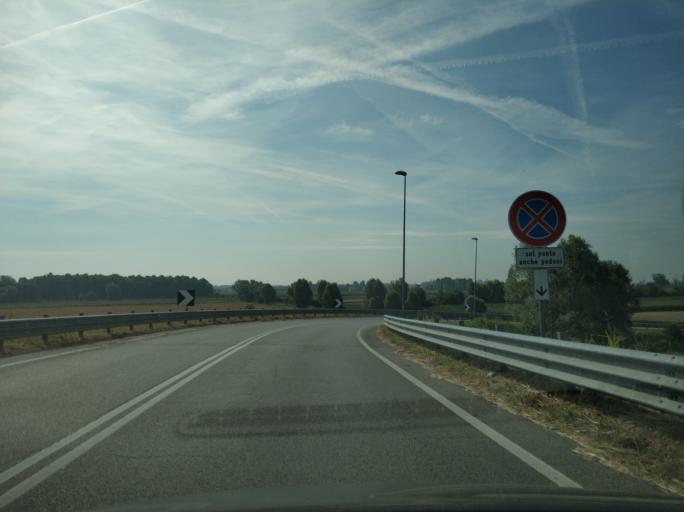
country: IT
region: Veneto
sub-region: Provincia di Padova
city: Sant'Elena
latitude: 45.2091
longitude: 11.6948
